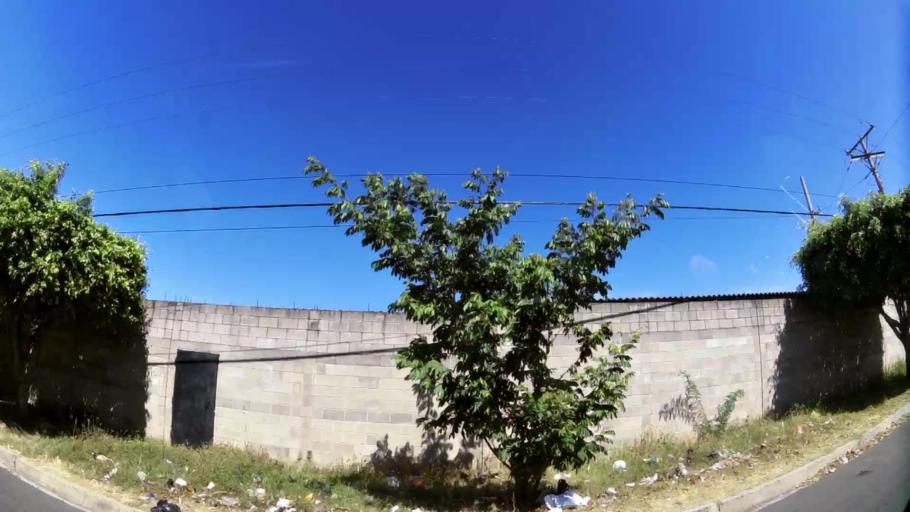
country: SV
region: Ahuachapan
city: Ahuachapan
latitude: 13.9290
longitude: -89.8400
